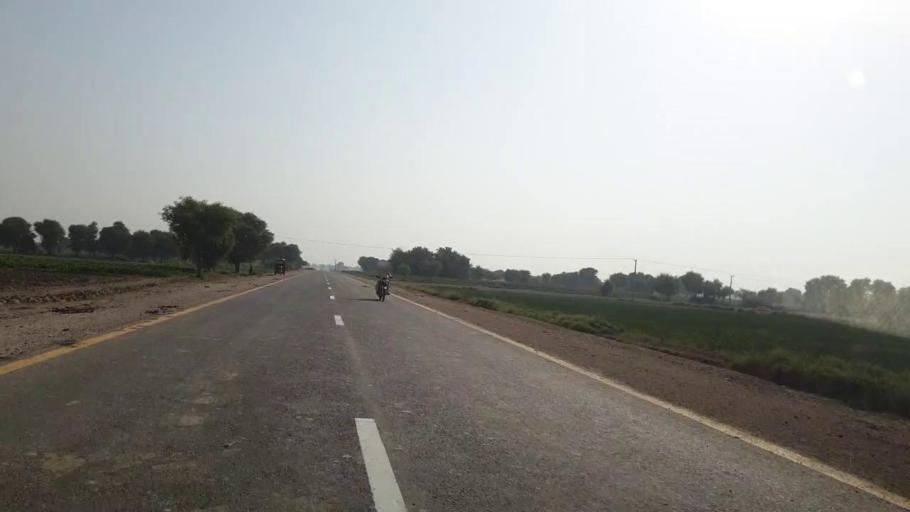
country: PK
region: Sindh
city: Bhan
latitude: 26.5211
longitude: 67.7877
